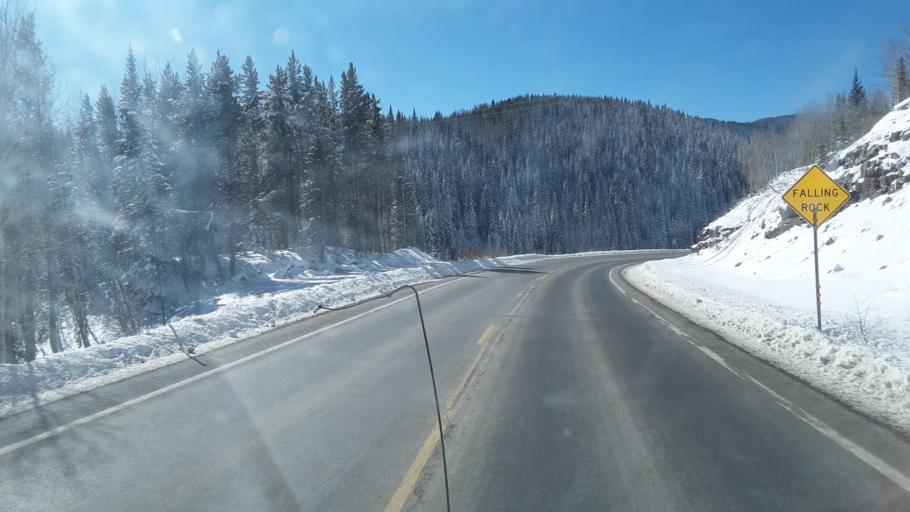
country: US
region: Colorado
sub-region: San Juan County
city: Silverton
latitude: 37.7268
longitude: -107.7347
